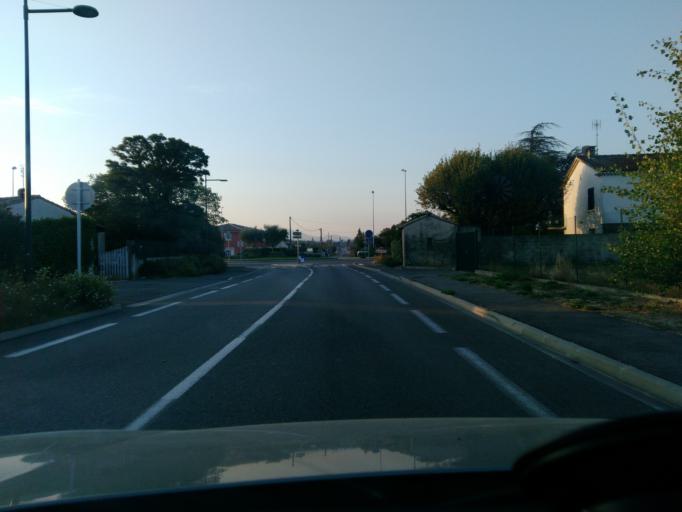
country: FR
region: Rhone-Alpes
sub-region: Departement de la Drome
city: Montelimar
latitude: 44.5321
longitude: 4.7518
